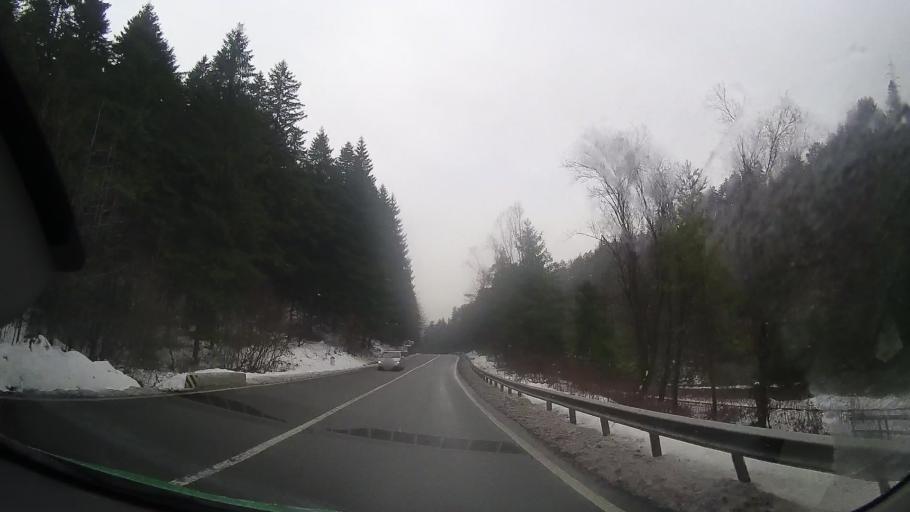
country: RO
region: Neamt
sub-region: Comuna Bicaz
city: Bicaz
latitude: 46.8956
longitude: 26.0467
